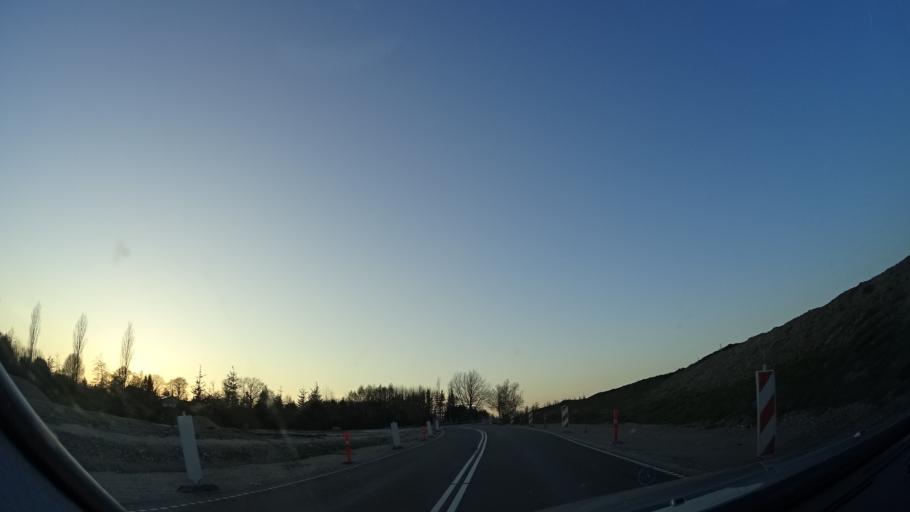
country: DK
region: Zealand
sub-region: Solrod Kommune
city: Solrod
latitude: 55.5225
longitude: 12.1840
